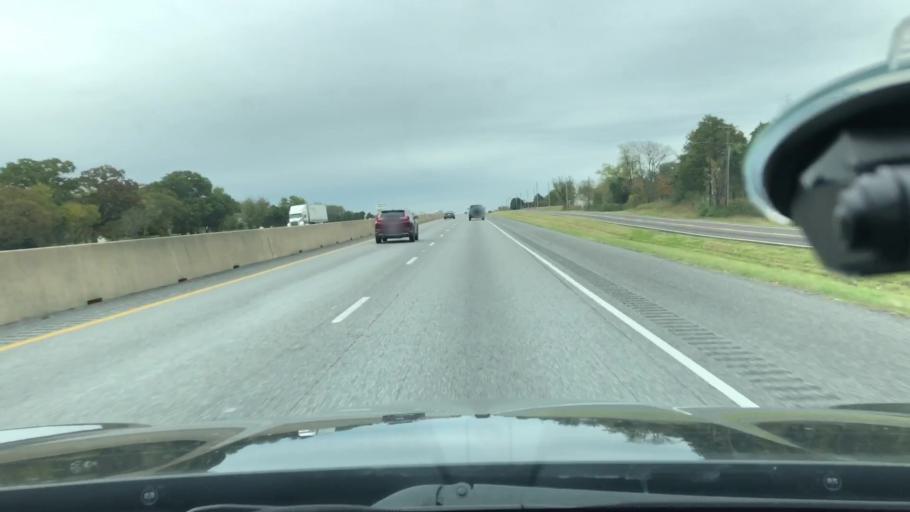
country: US
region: Texas
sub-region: Hunt County
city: Greenville
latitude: 33.1333
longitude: -96.0417
